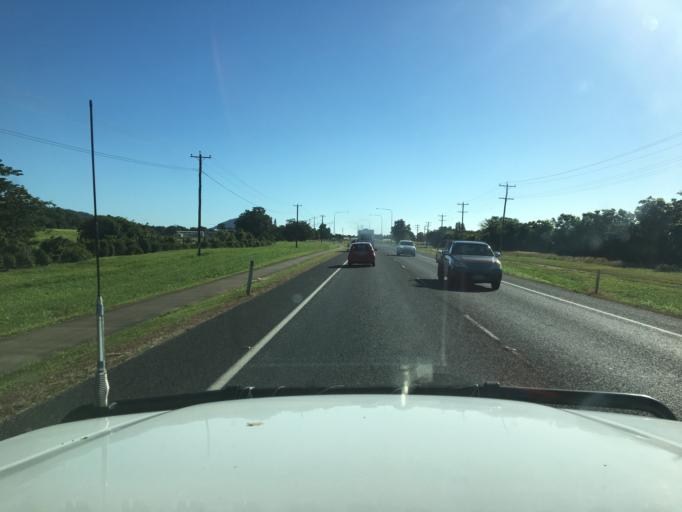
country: AU
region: Queensland
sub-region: Cairns
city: Redlynch
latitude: -16.8588
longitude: 145.6945
